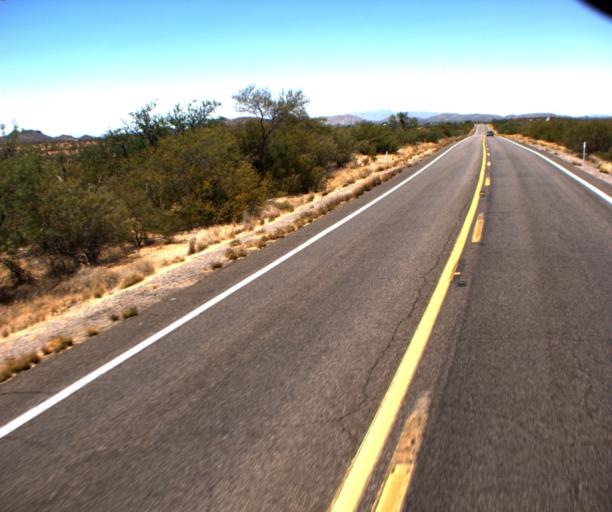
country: US
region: Arizona
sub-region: Pima County
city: Catalina
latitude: 32.6466
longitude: -111.0220
